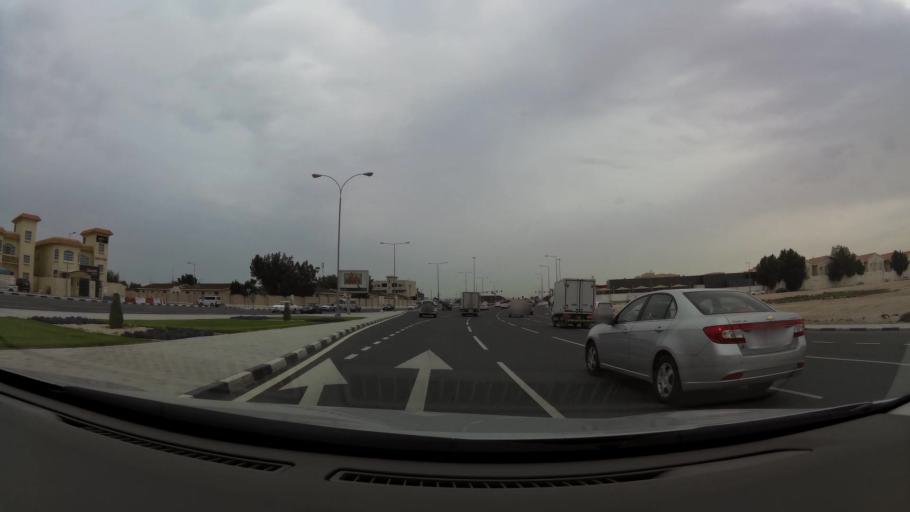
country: QA
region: Baladiyat ad Dawhah
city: Doha
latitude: 25.3249
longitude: 51.4860
